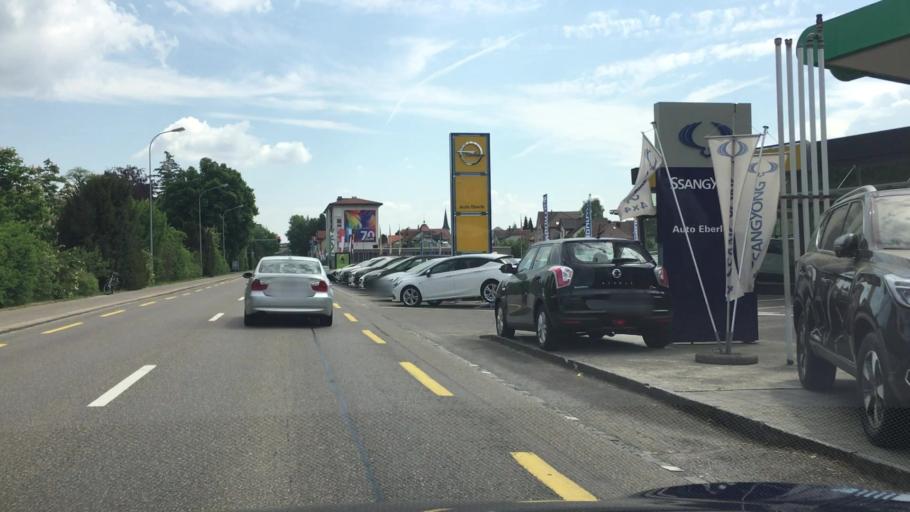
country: CH
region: Saint Gallen
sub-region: Wahlkreis Wil
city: Wil
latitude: 47.4651
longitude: 9.0345
